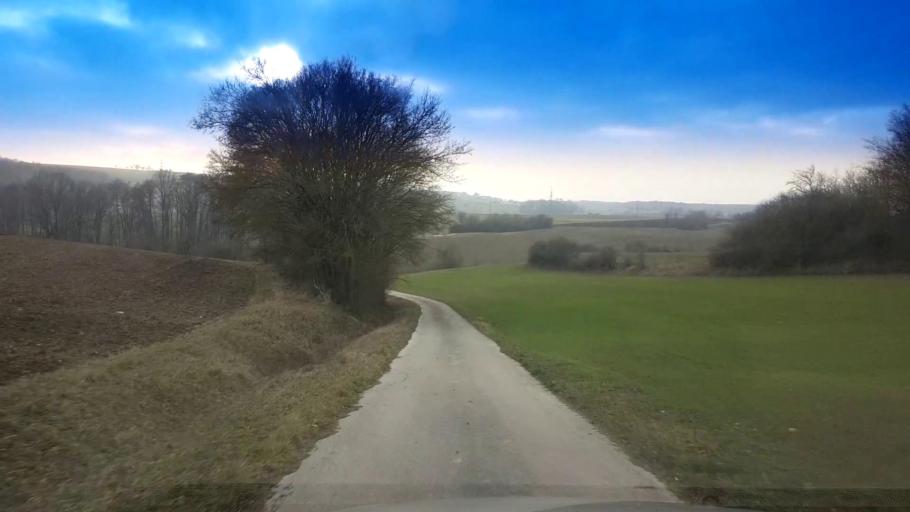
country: DE
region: Bavaria
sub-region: Upper Franconia
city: Hallerndorf
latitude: 49.7793
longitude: 10.9766
